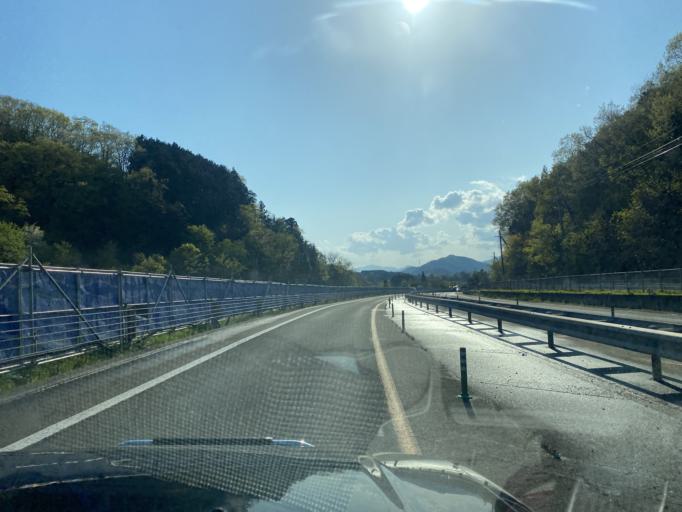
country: JP
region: Kyoto
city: Ayabe
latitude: 35.3226
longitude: 135.2482
